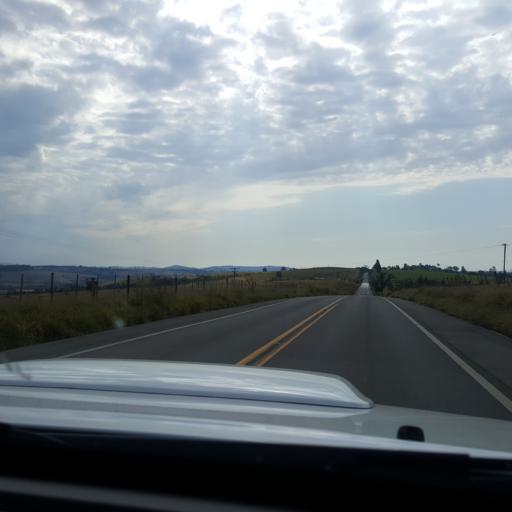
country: BR
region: Sao Paulo
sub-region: Itaporanga
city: Itaporanga
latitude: -23.7626
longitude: -49.4482
